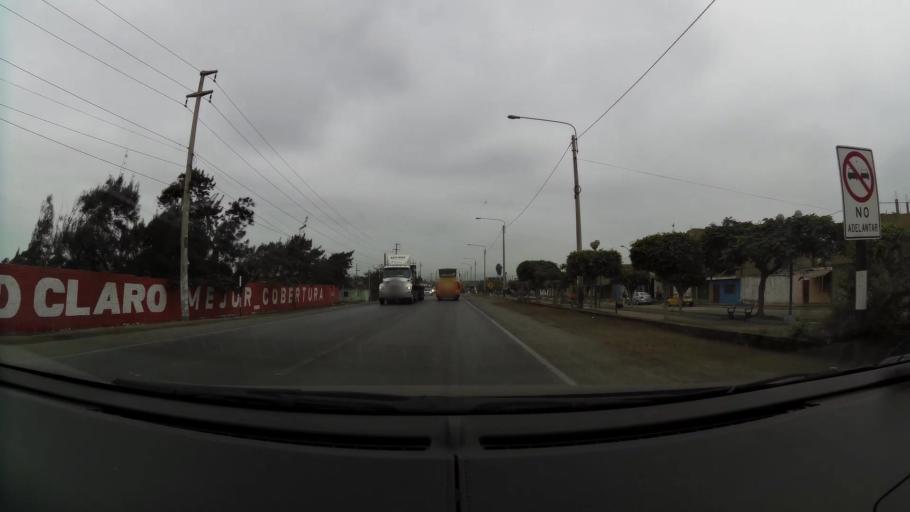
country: PE
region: Ancash
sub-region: Provincia de Santa
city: Santa
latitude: -8.9865
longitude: -78.6171
